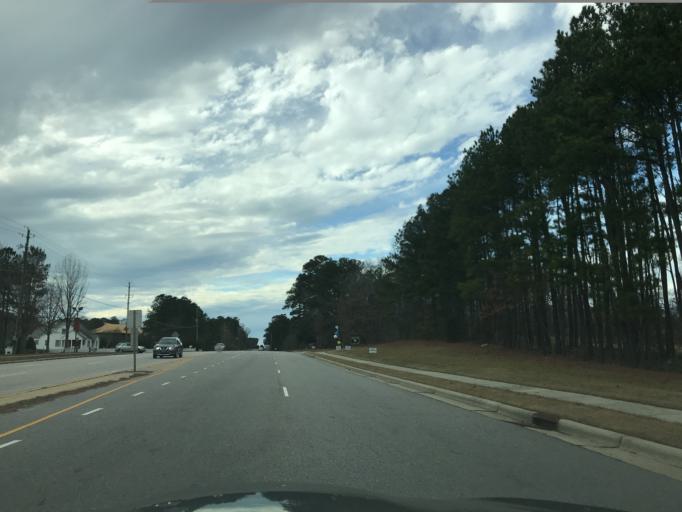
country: US
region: North Carolina
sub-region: Wake County
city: Knightdale
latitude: 35.8561
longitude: -78.5560
